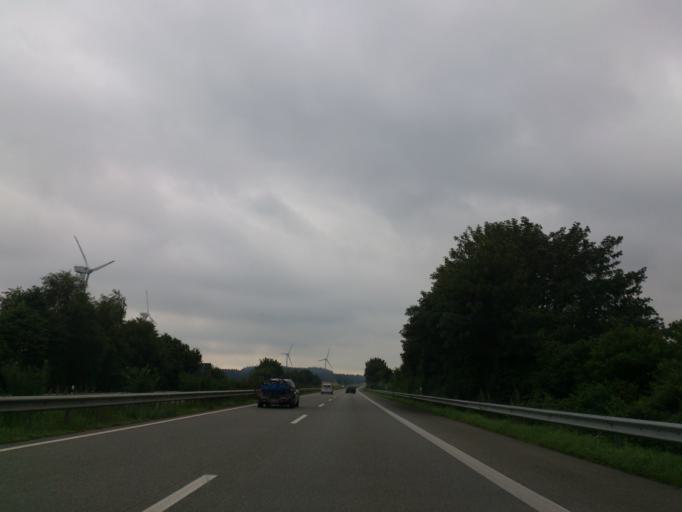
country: DE
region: Schleswig-Holstein
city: Bokelrehm
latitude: 54.0539
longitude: 9.3810
